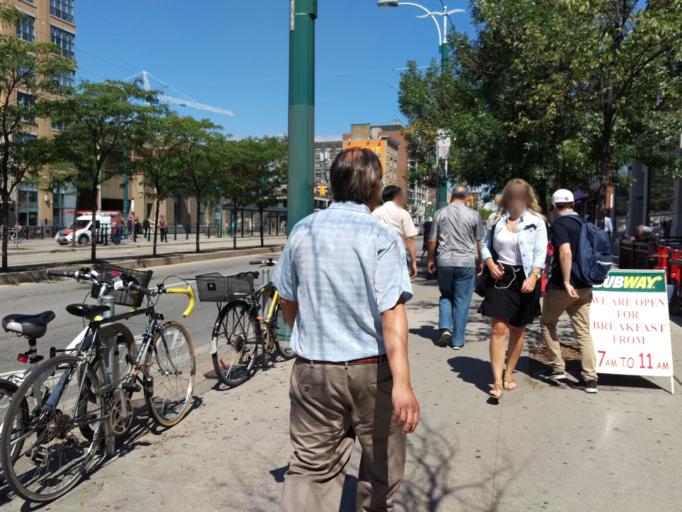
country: CA
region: Ontario
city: Toronto
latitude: 43.6480
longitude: -79.3960
